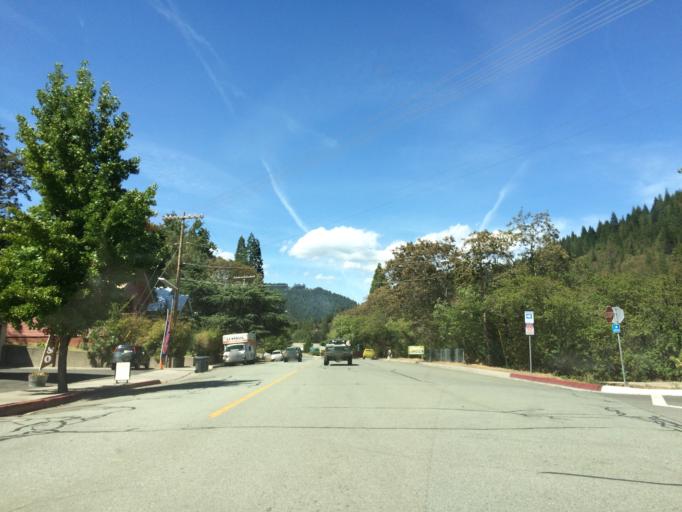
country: US
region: California
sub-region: Siskiyou County
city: Dunsmuir
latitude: 41.2155
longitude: -122.2726
